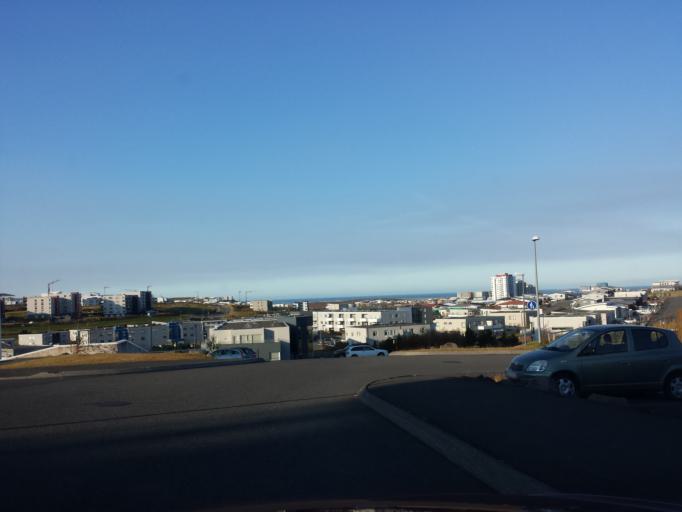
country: IS
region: Capital Region
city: Reykjavik
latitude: 64.0864
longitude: -21.8223
